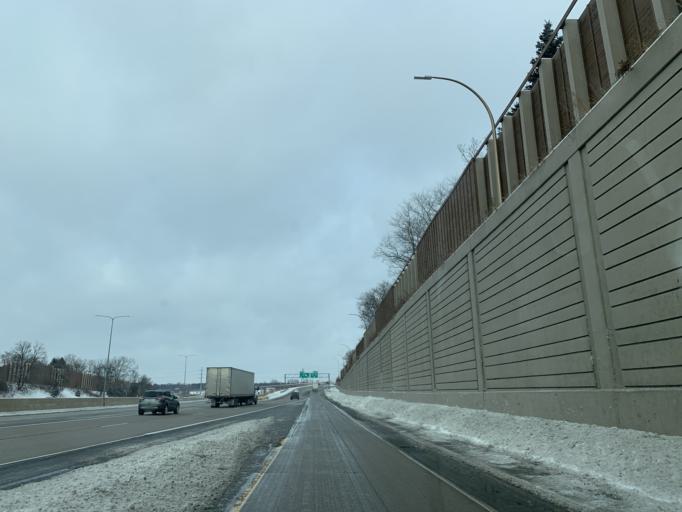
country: US
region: Minnesota
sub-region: Ramsey County
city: Little Canada
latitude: 45.0279
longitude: -93.0893
